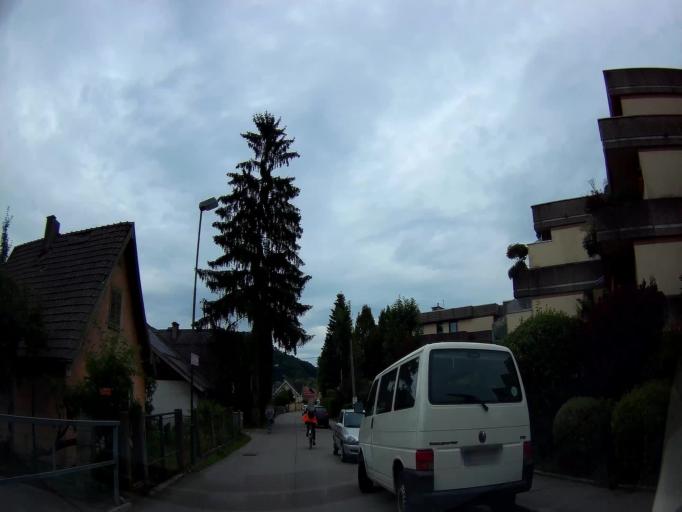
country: AT
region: Salzburg
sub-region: Politischer Bezirk Salzburg-Umgebung
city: Hallwang
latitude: 47.8271
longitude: 13.0658
